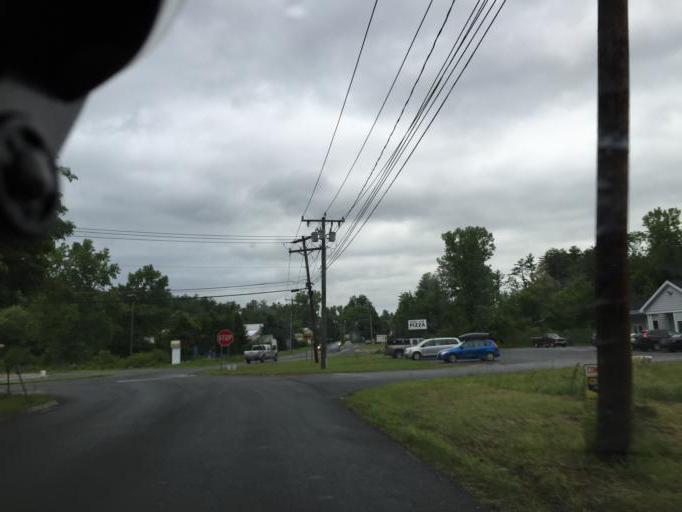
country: US
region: Connecticut
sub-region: Litchfield County
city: Canaan
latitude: 42.0363
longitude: -73.3251
